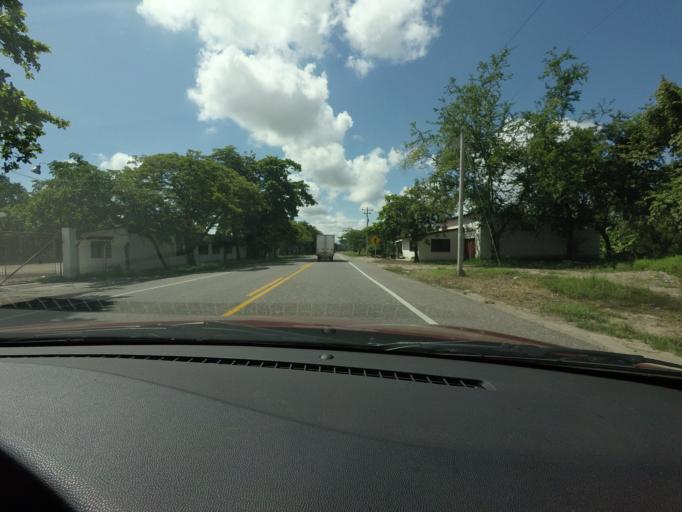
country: CO
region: Tolima
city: Saldana
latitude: 3.9435
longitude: -75.0115
